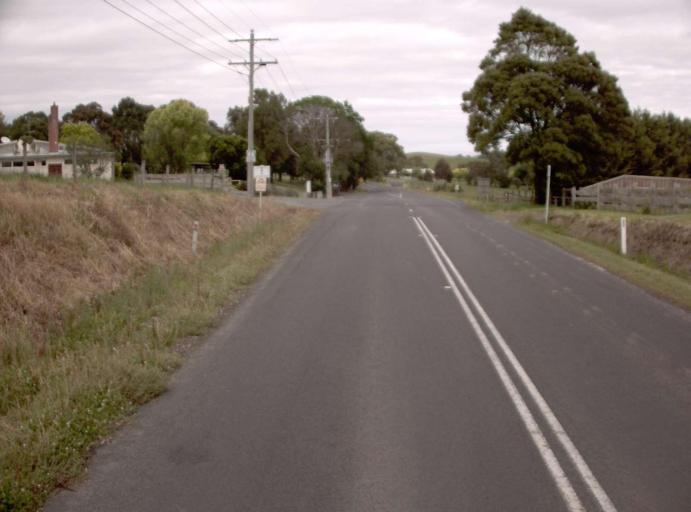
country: AU
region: Victoria
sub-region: Bass Coast
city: North Wonthaggi
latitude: -38.4430
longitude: 145.8066
